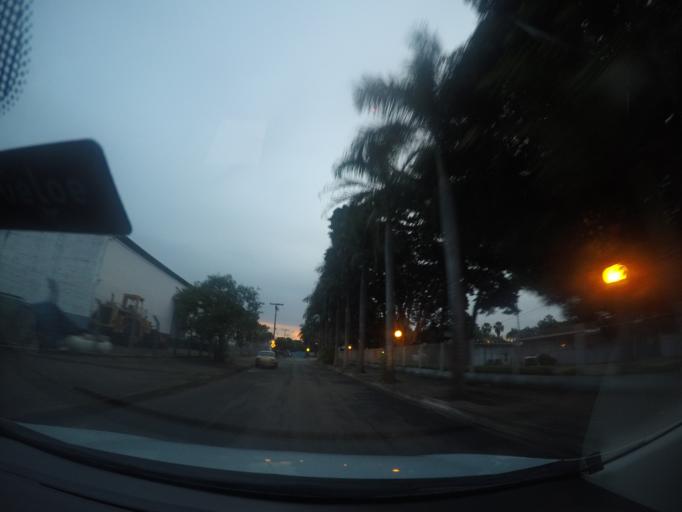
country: BR
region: Goias
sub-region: Goiania
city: Goiania
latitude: -16.6401
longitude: -49.2425
